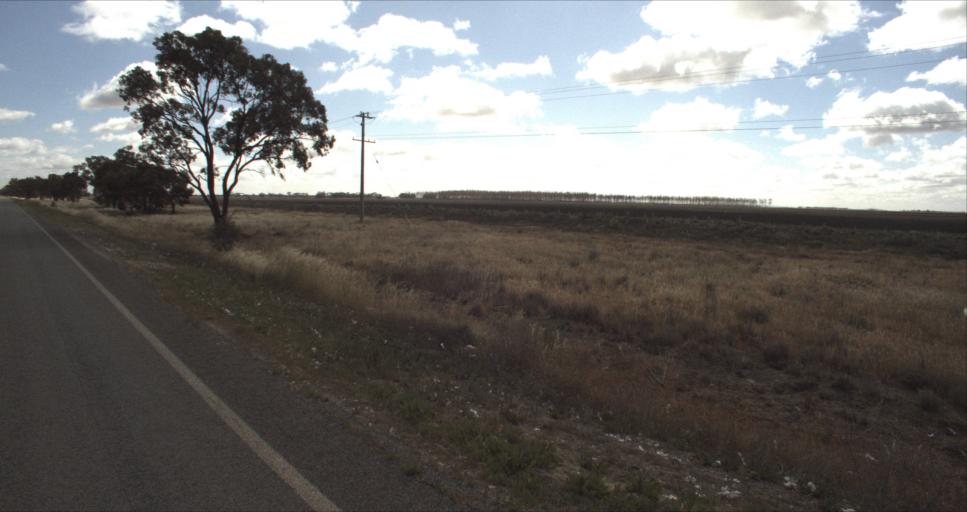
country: AU
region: New South Wales
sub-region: Murrumbidgee Shire
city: Darlington Point
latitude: -34.5687
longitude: 146.1676
